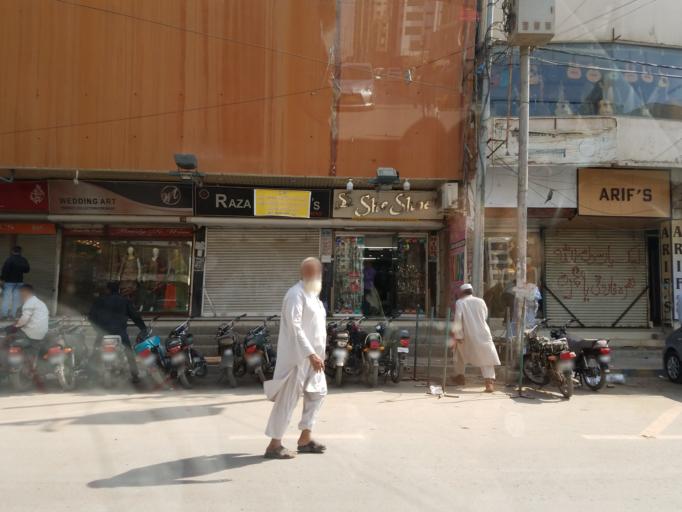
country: PK
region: Sindh
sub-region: Karachi District
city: Karachi
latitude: 24.8756
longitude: 67.0625
